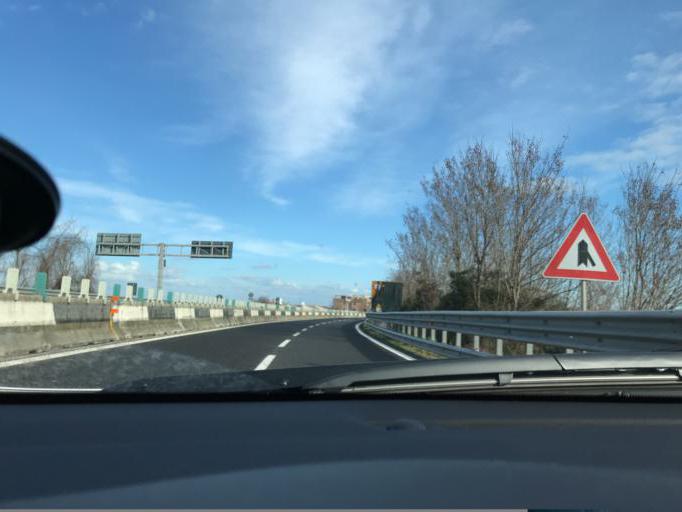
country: IT
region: The Marches
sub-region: Provincia di Ancona
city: Camerata Picena
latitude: 43.5954
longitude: 13.3519
